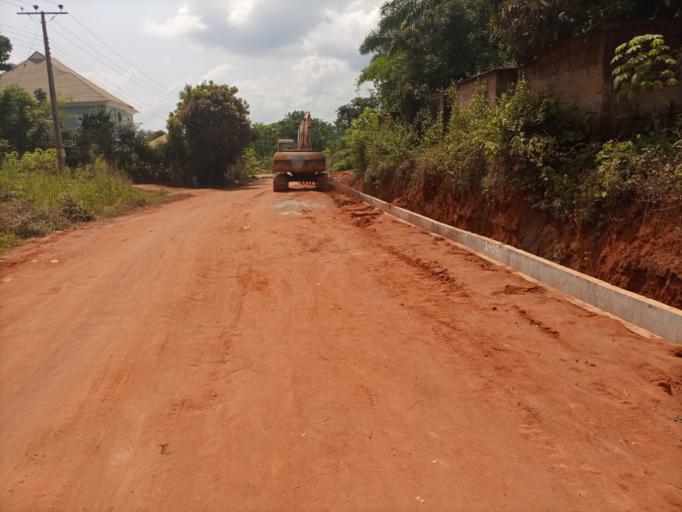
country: NG
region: Abia
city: Umuahia
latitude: 5.4829
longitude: 7.3307
